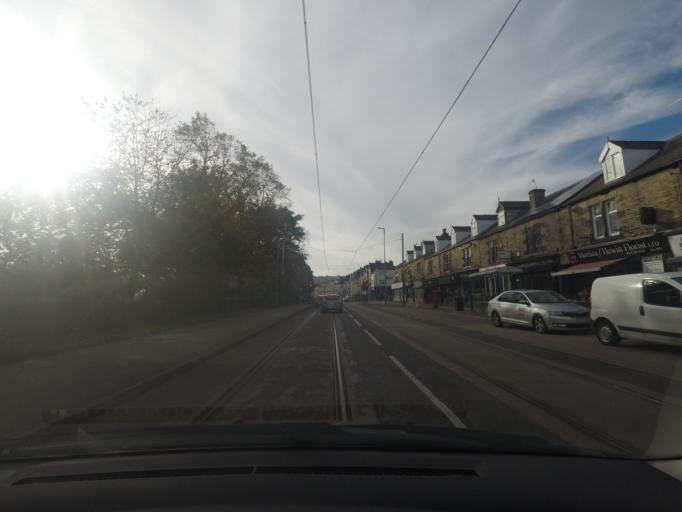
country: GB
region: England
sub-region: Sheffield
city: Oughtibridge
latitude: 53.4076
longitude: -1.5041
